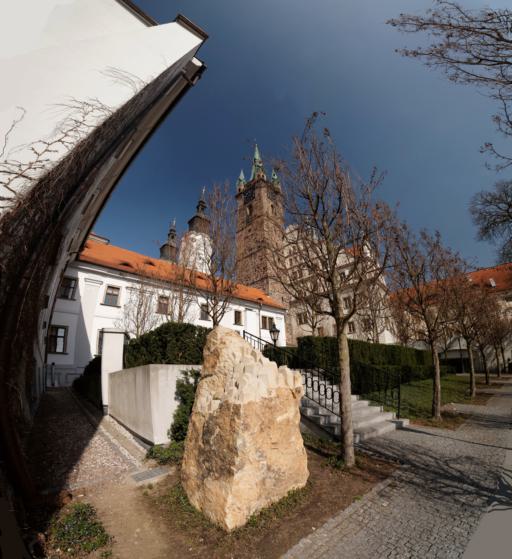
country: CZ
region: Plzensky
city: Klatovy
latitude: 49.3944
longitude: 13.2922
